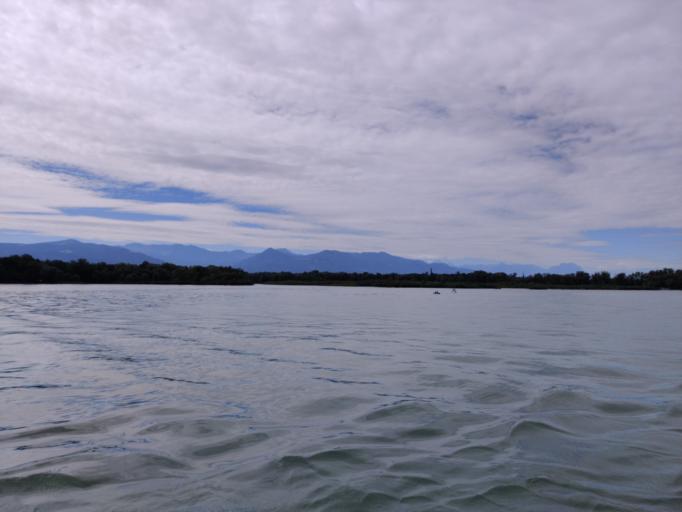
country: AT
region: Vorarlberg
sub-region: Politischer Bezirk Bregenz
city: Hard
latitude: 47.5103
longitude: 9.6936
